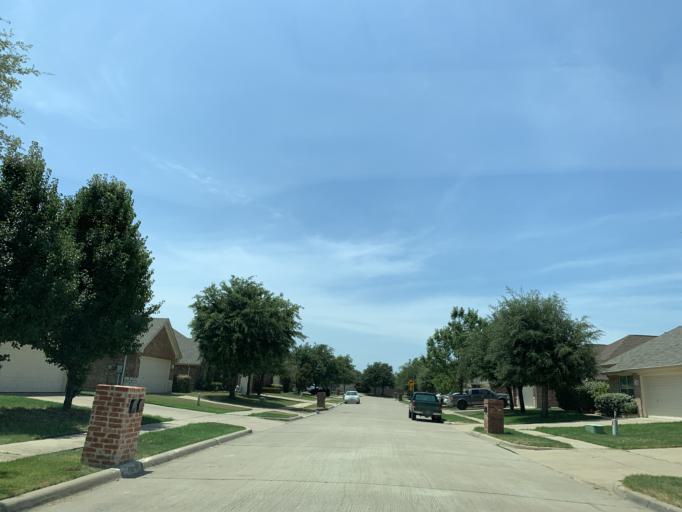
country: US
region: Texas
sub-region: Dallas County
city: Cedar Hill
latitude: 32.6440
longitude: -97.0262
